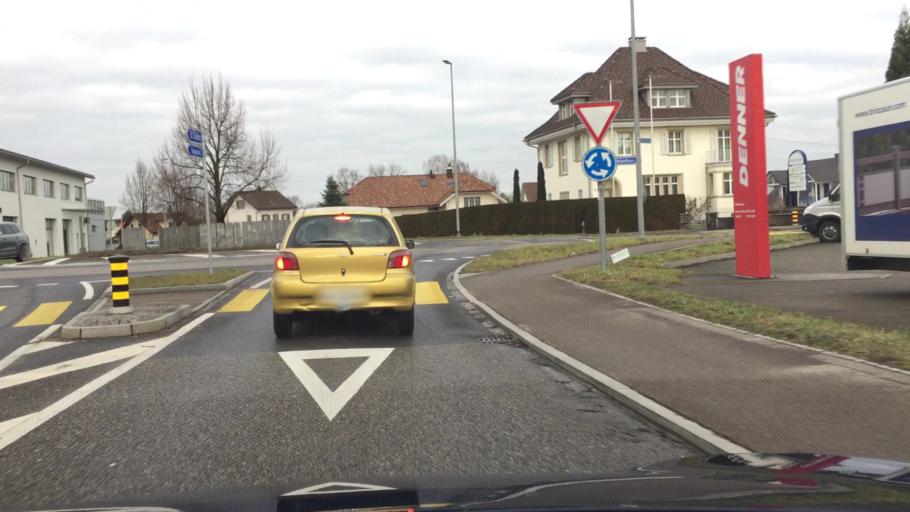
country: CH
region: Thurgau
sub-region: Arbon District
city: Amriswil
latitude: 47.5442
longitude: 9.2855
